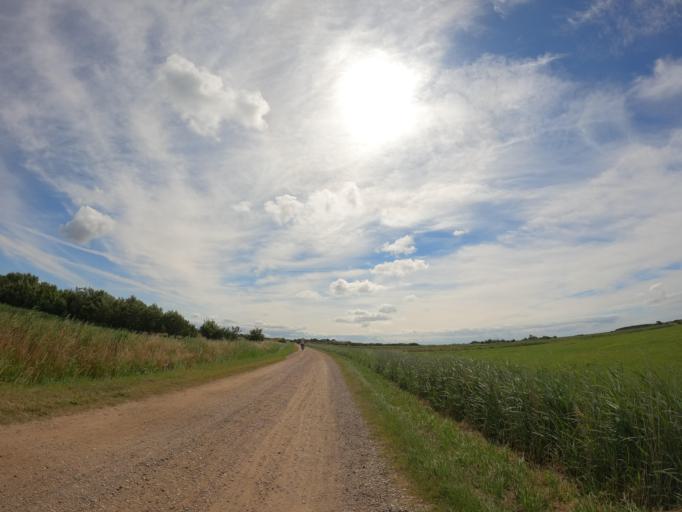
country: DE
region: Schleswig-Holstein
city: Tinnum
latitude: 54.8946
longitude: 8.3482
